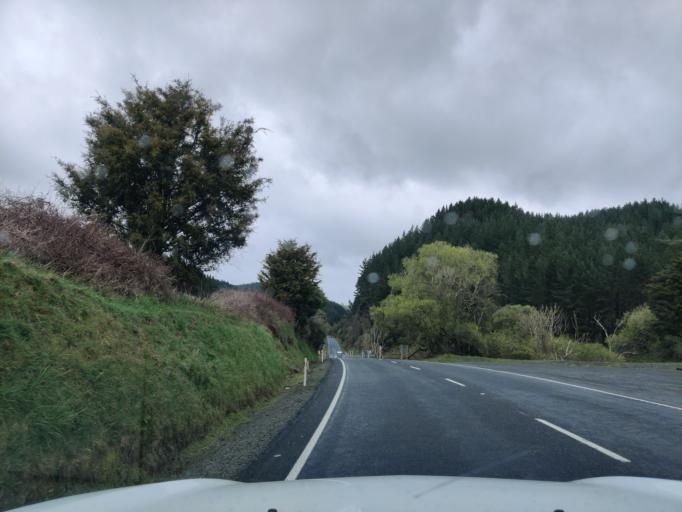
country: NZ
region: Waikato
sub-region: Otorohanga District
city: Otorohanga
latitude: -38.6517
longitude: 175.2078
